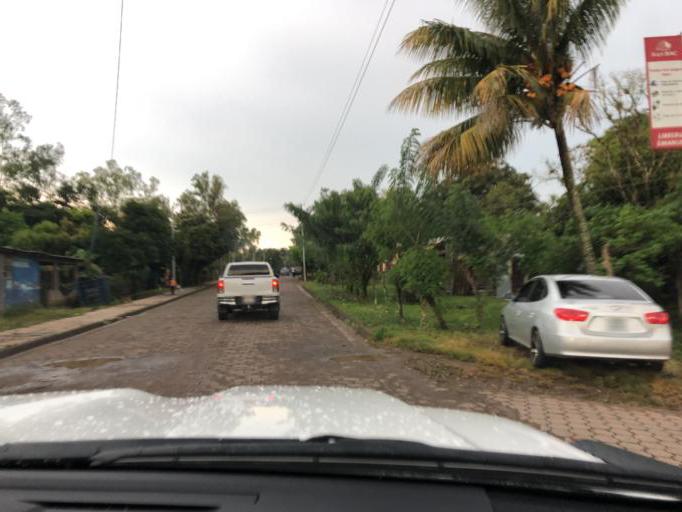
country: NI
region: Chontales
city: La Libertad
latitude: 12.2121
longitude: -85.1677
